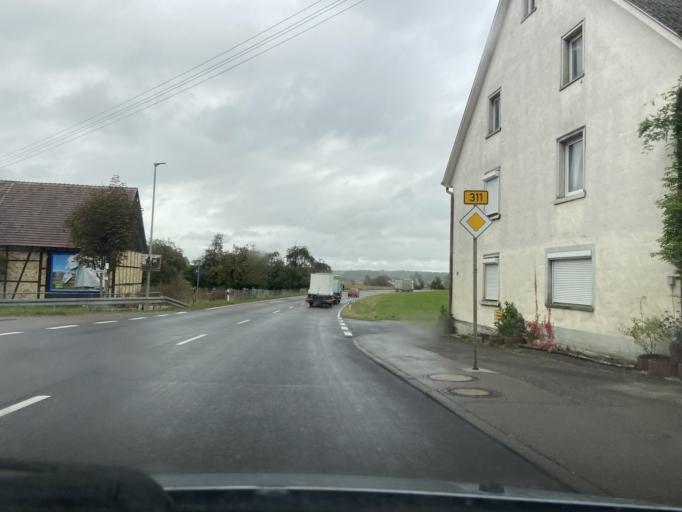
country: DE
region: Baden-Wuerttemberg
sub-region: Tuebingen Region
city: Messkirch
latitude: 48.0044
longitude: 9.1588
